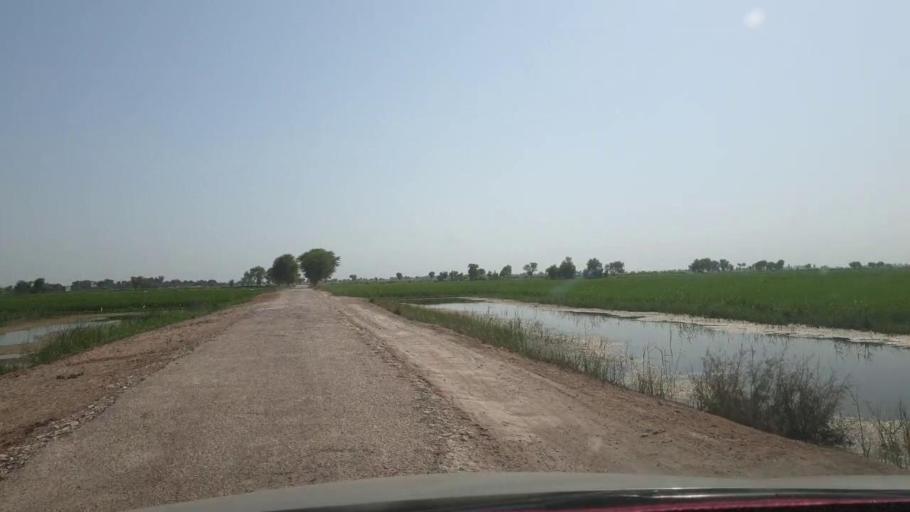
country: PK
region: Sindh
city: Nasirabad
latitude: 27.3656
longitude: 67.8527
